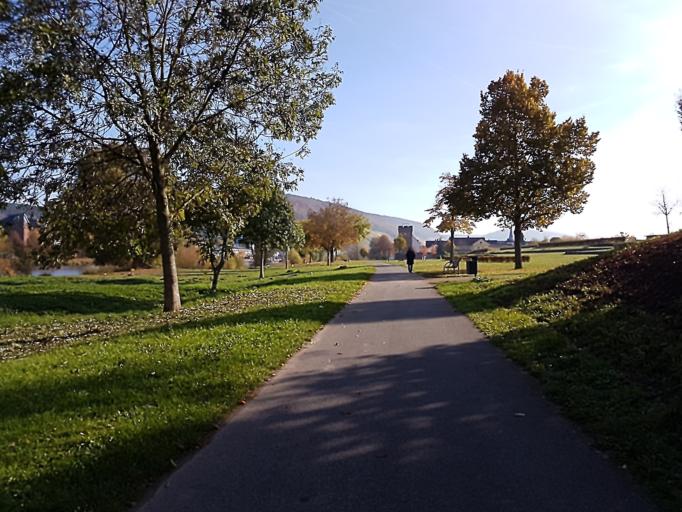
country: DE
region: Bavaria
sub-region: Regierungsbezirk Unterfranken
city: Worth am Main
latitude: 49.8003
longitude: 9.1529
